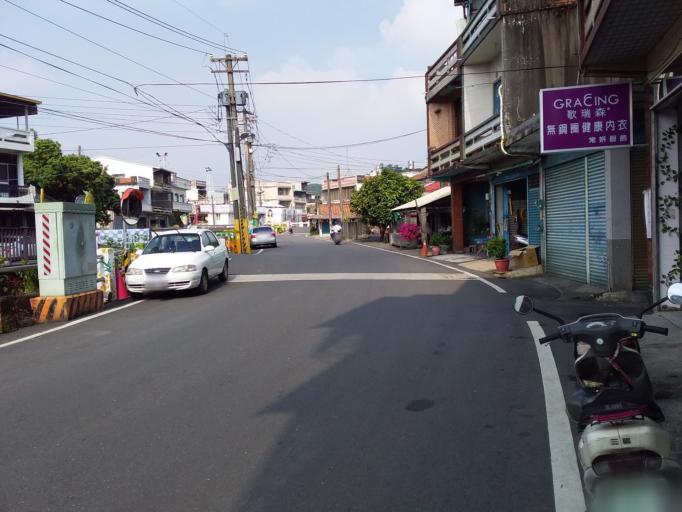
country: TW
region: Taiwan
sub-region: Pingtung
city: Pingtung
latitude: 22.6875
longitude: 120.4132
